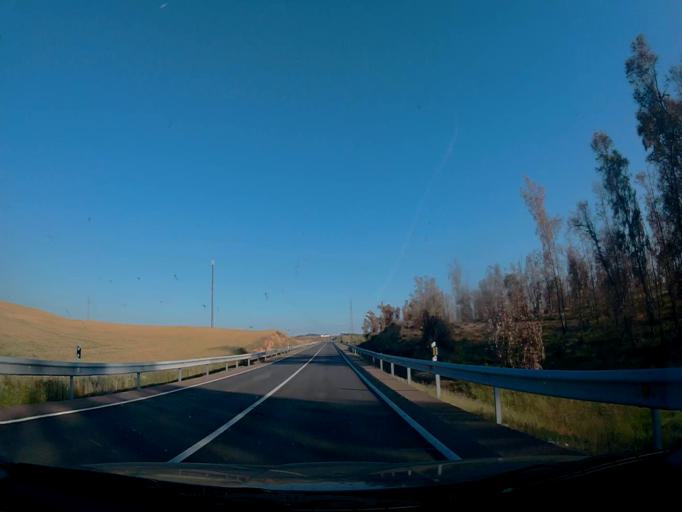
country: ES
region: Castille-La Mancha
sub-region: Province of Toledo
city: Hormigos
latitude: 40.1164
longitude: -4.4051
